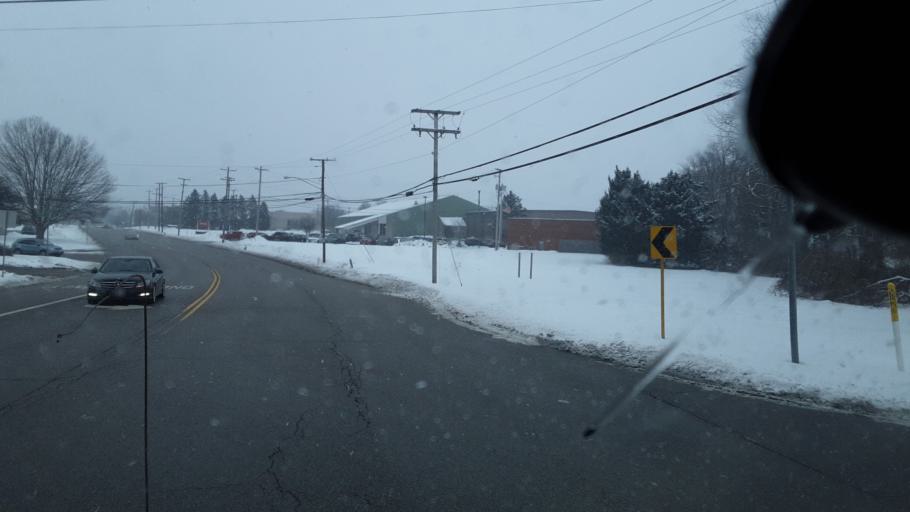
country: US
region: Ohio
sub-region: Licking County
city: Heath
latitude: 40.0406
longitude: -82.4698
